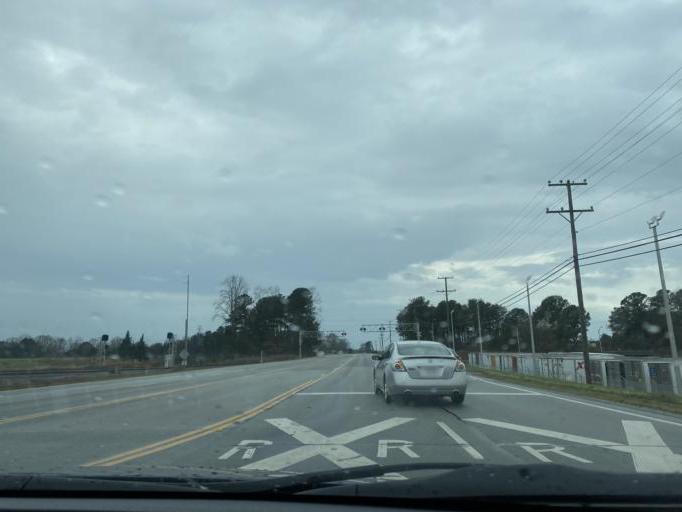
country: US
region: South Carolina
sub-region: Cherokee County
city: Gaffney
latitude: 35.0527
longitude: -81.6875
